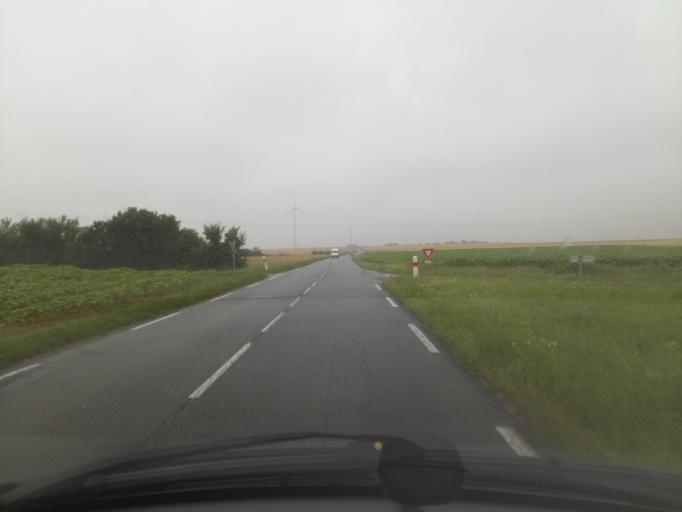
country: FR
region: Poitou-Charentes
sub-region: Departement de la Charente-Maritime
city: Saint-Jean-de-Liversay
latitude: 46.2492
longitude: -0.8815
